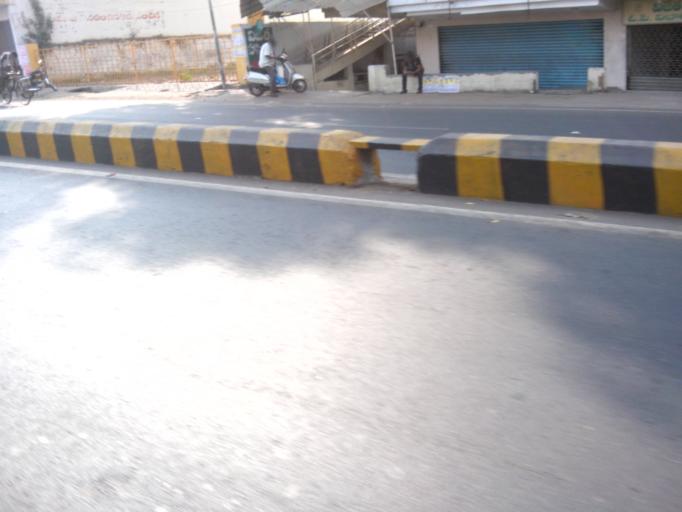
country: IN
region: Andhra Pradesh
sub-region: Krishna
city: Vijayawada
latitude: 16.5149
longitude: 80.6350
